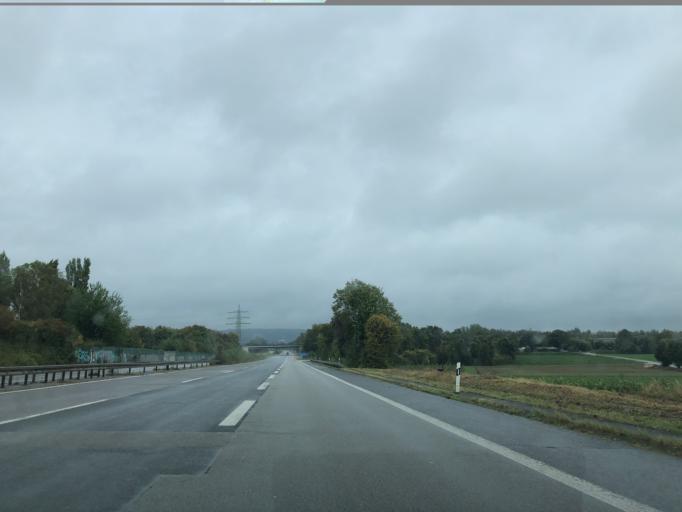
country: DE
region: North Rhine-Westphalia
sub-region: Regierungsbezirk Dusseldorf
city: Grevenbroich
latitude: 51.0904
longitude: 6.5493
